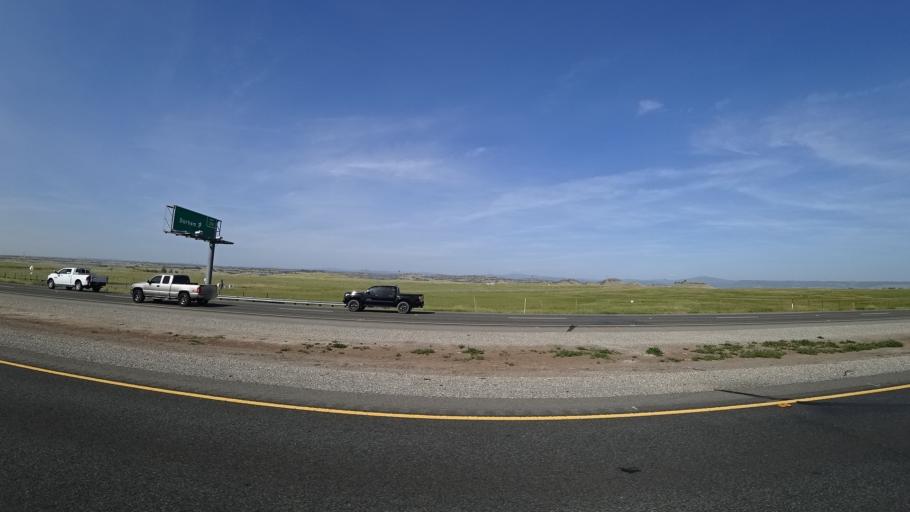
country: US
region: California
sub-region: Butte County
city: Durham
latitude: 39.6385
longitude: -121.7120
